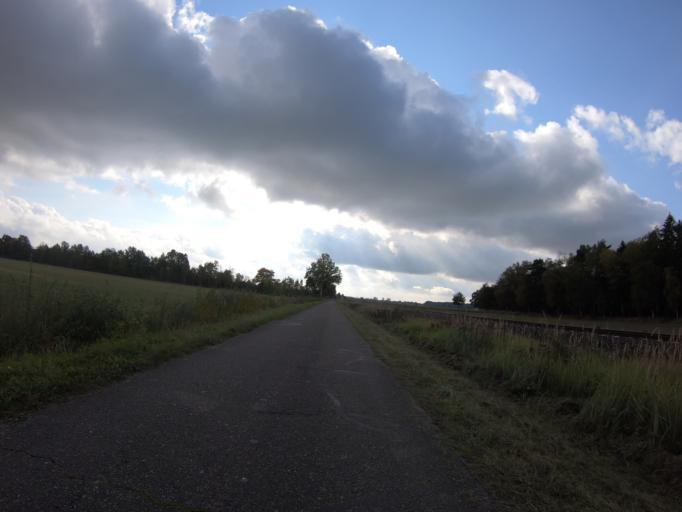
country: DE
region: Lower Saxony
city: Wahrenholz
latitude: 52.5881
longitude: 10.6095
